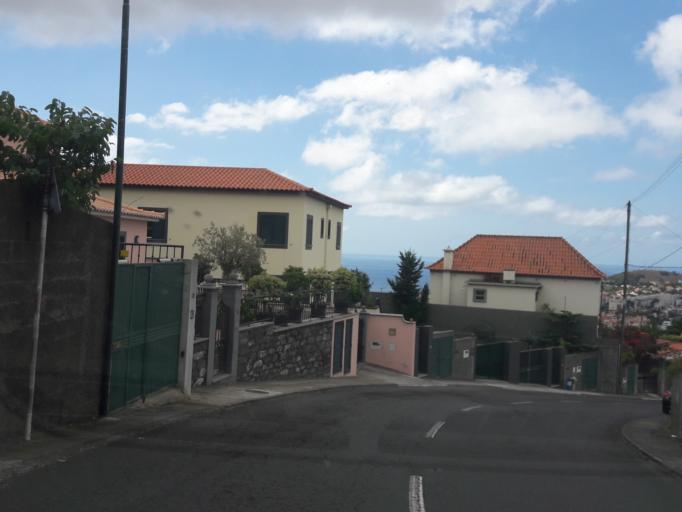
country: PT
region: Madeira
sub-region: Funchal
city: Nossa Senhora do Monte
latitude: 32.6695
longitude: -16.9269
